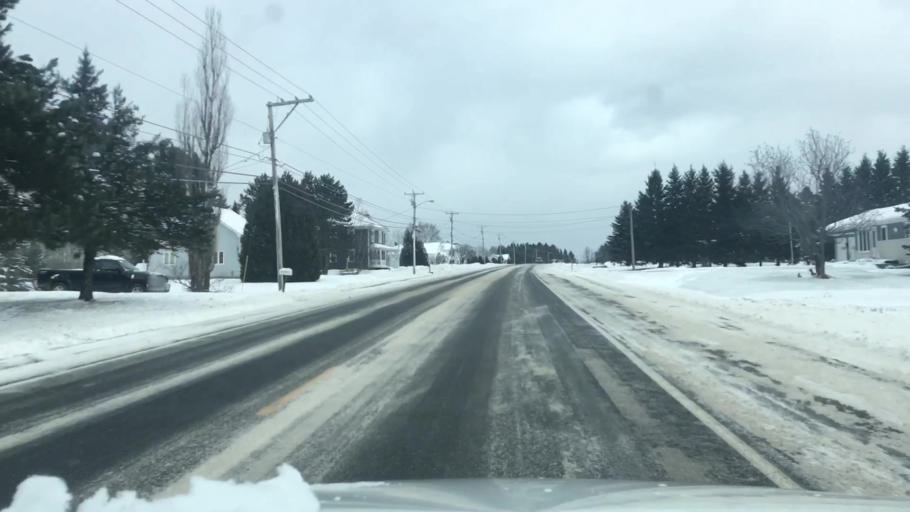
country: US
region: Maine
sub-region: Aroostook County
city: Madawaska
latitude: 47.3444
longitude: -68.2455
